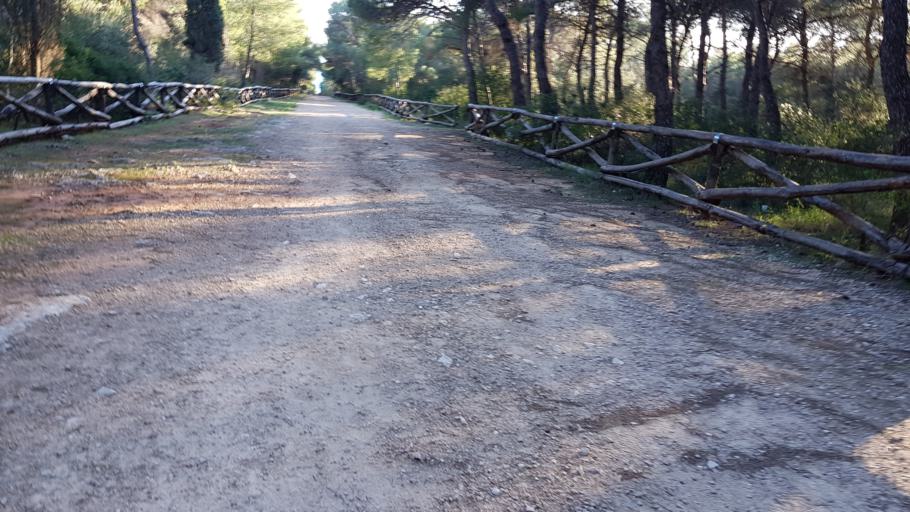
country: IT
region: Apulia
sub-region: Provincia di Lecce
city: Nardo
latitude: 40.1519
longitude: 17.9711
